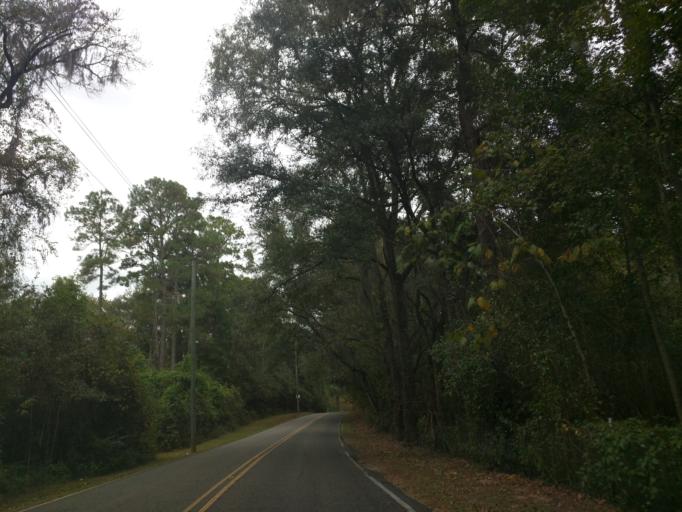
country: US
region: Florida
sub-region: Leon County
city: Tallahassee
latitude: 30.4196
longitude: -84.2101
